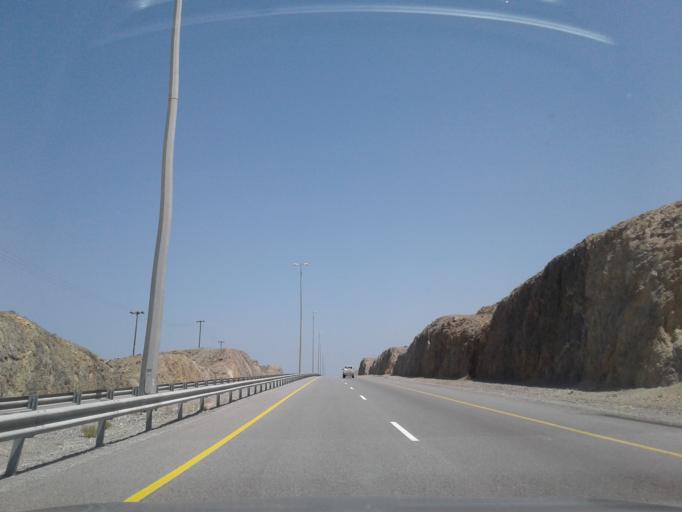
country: OM
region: Muhafazat Masqat
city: Muscat
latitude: 23.2045
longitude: 58.8163
